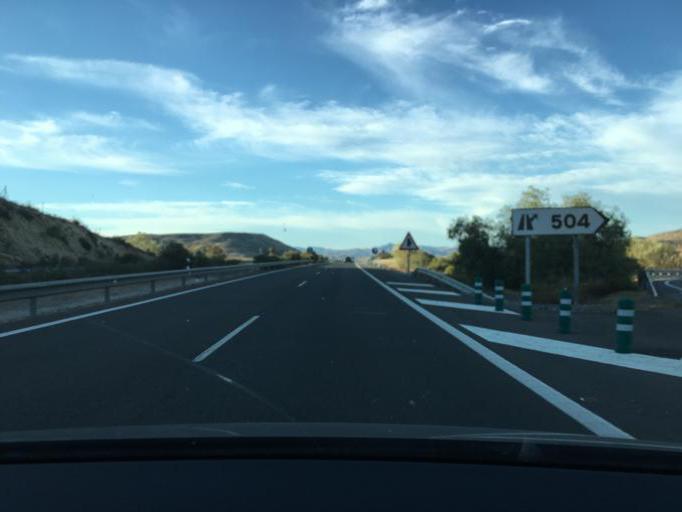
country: ES
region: Andalusia
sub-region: Provincia de Almeria
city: Sorbas
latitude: 37.0642
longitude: -2.0537
